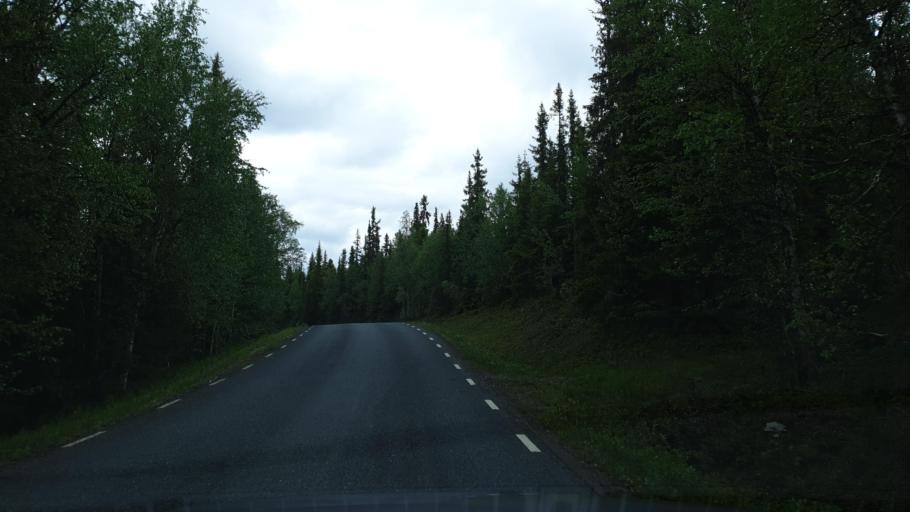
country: SE
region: Vaesterbotten
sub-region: Vilhelmina Kommun
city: Sjoberg
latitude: 65.2731
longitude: 15.3689
